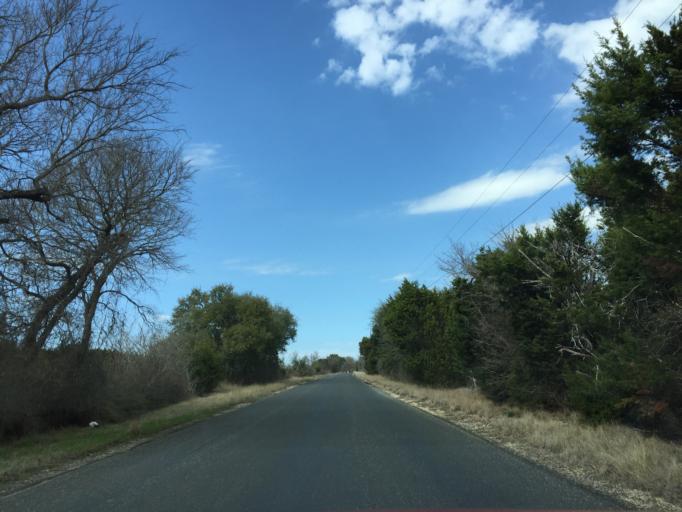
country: US
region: Texas
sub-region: Burnet County
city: Bertram
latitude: 30.7440
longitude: -97.9391
